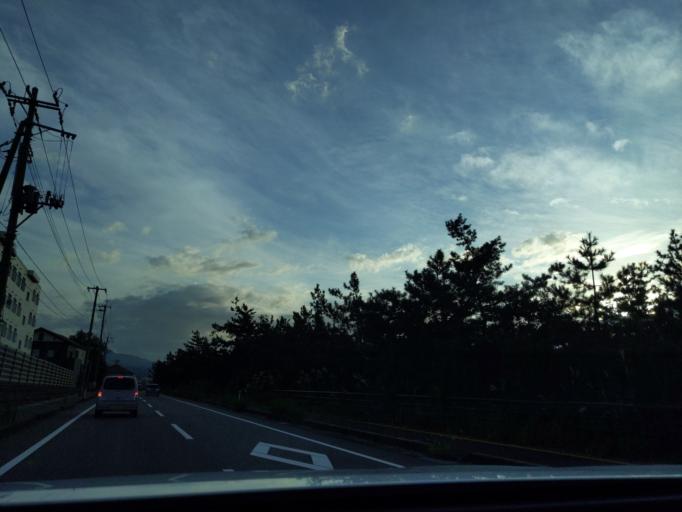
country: JP
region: Niigata
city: Kashiwazaki
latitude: 37.3787
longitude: 138.5571
